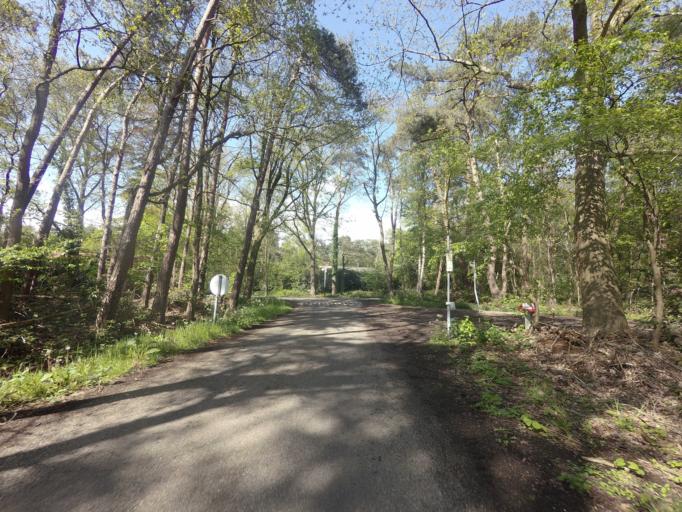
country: NL
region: Overijssel
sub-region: Gemeente Haaksbergen
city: Haaksbergen
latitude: 52.1689
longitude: 6.8040
